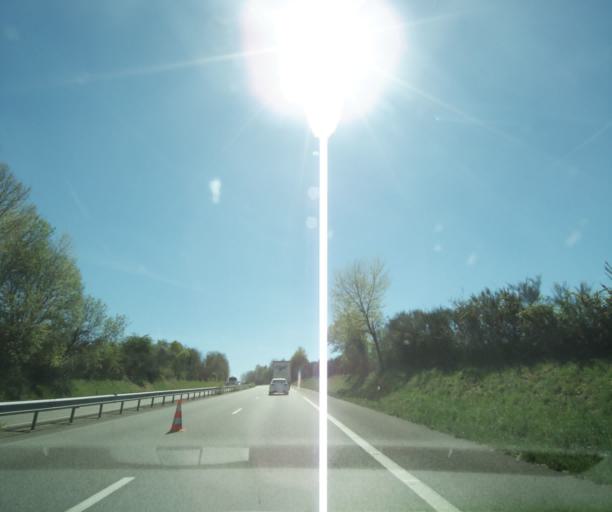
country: FR
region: Limousin
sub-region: Departement de la Haute-Vienne
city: Saint-Germain-les-Belles
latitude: 45.6066
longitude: 1.4475
